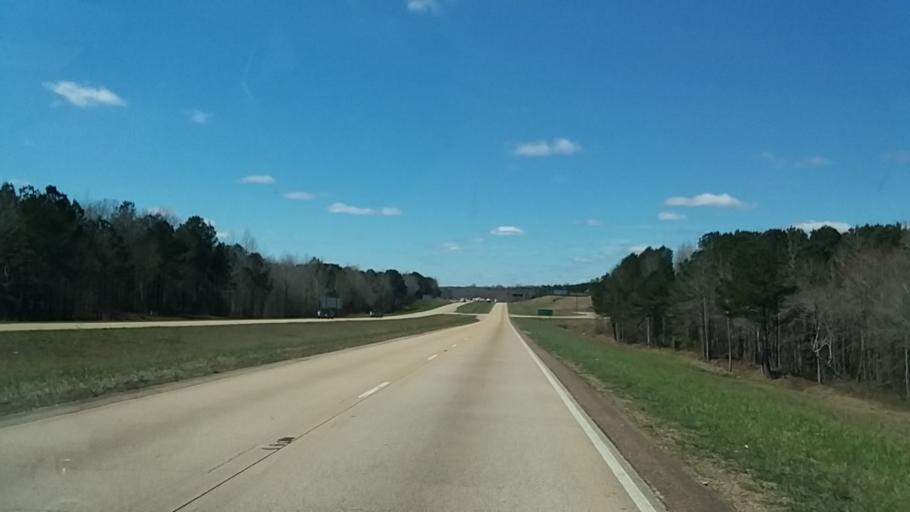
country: US
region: Mississippi
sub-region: Tishomingo County
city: Iuka
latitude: 34.7986
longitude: -88.2222
